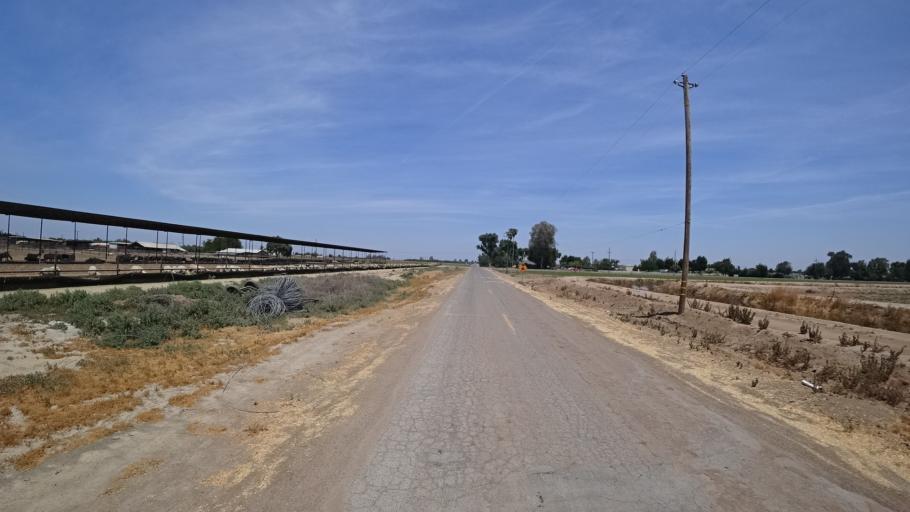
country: US
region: California
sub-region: Fresno County
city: Riverdale
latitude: 36.4004
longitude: -119.8162
